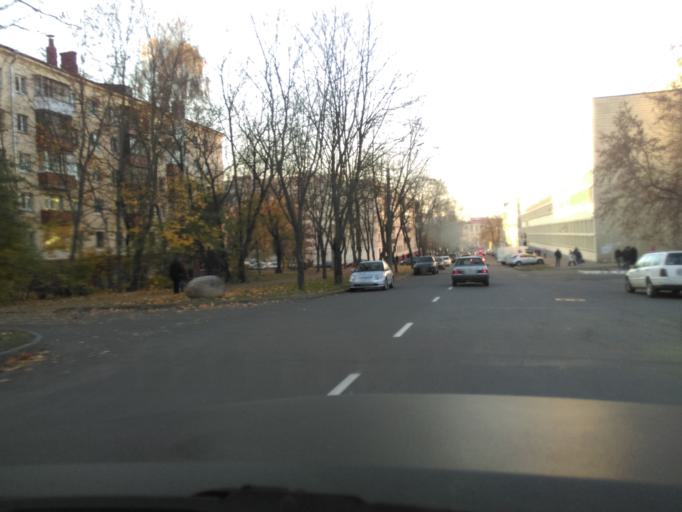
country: BY
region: Minsk
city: Minsk
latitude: 53.9135
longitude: 27.5914
